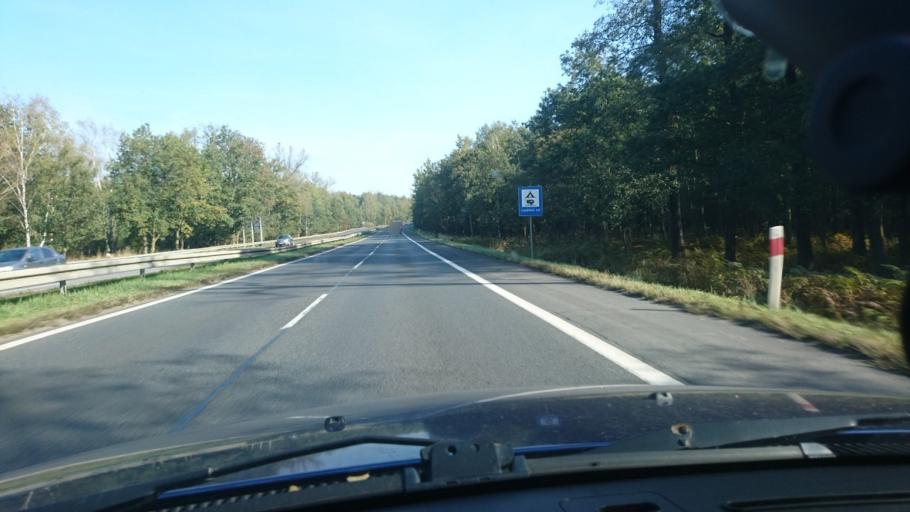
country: PL
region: Silesian Voivodeship
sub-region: Katowice
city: Murcki
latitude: 50.1750
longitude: 19.0234
